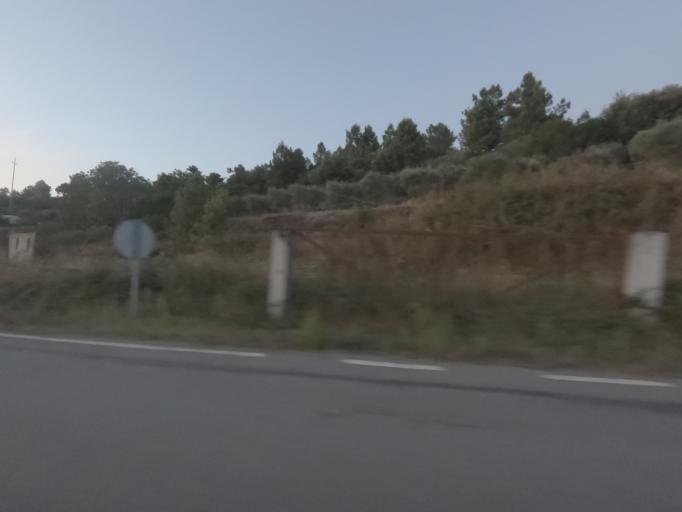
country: PT
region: Viseu
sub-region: Armamar
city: Armamar
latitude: 41.2002
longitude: -7.6973
